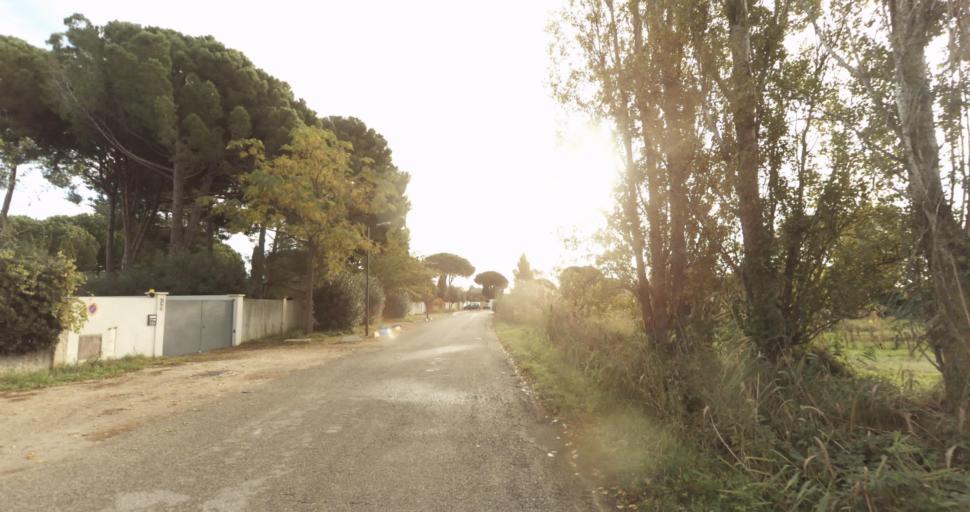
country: FR
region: Languedoc-Roussillon
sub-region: Departement du Gard
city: Aigues-Mortes
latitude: 43.5643
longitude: 4.1986
